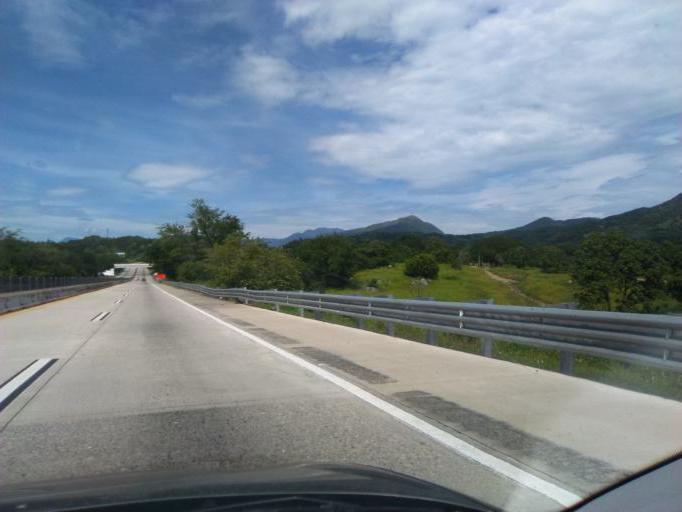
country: MX
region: Guerrero
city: Tierra Colorada
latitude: 17.1616
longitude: -99.5529
